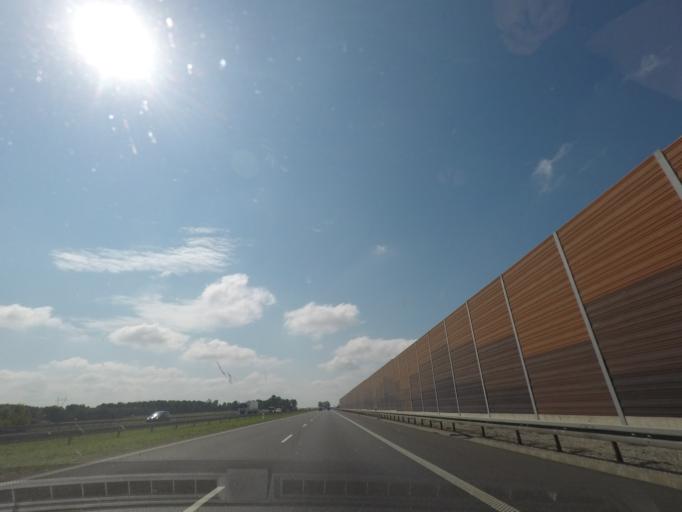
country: PL
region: Kujawsko-Pomorskie
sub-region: Powiat aleksandrowski
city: Waganiec
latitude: 52.7840
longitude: 18.8424
